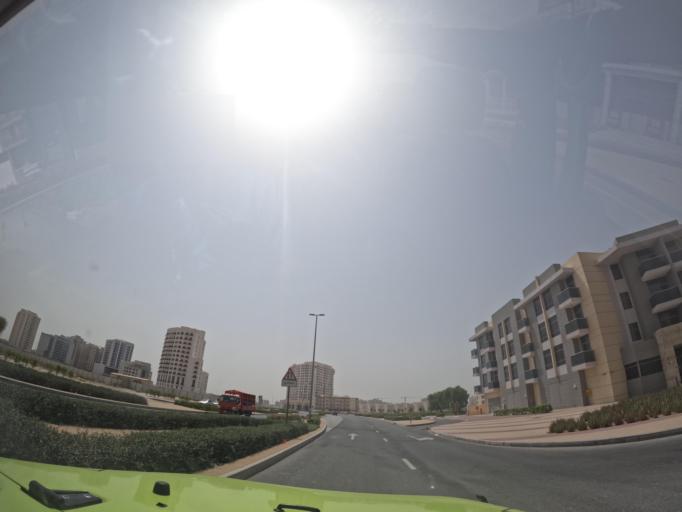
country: AE
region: Dubai
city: Dubai
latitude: 25.0983
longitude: 55.3776
